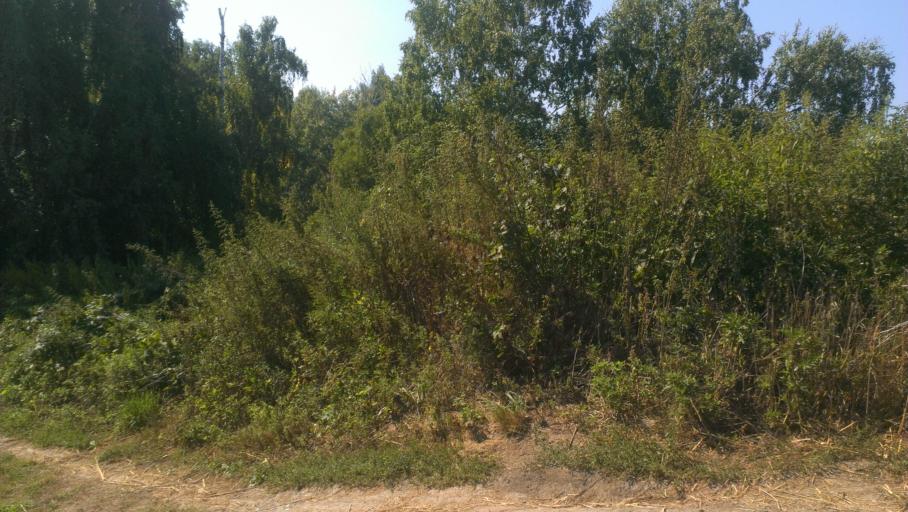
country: RU
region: Altai Krai
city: Nauchnyy Gorodok
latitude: 53.4249
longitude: 83.5059
